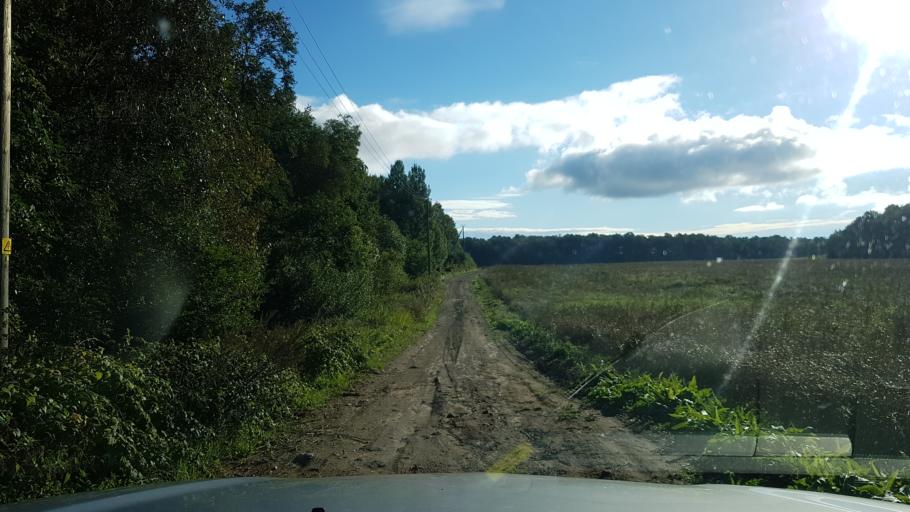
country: EE
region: Harju
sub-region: Rae vald
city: Jueri
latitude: 59.3464
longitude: 24.8734
